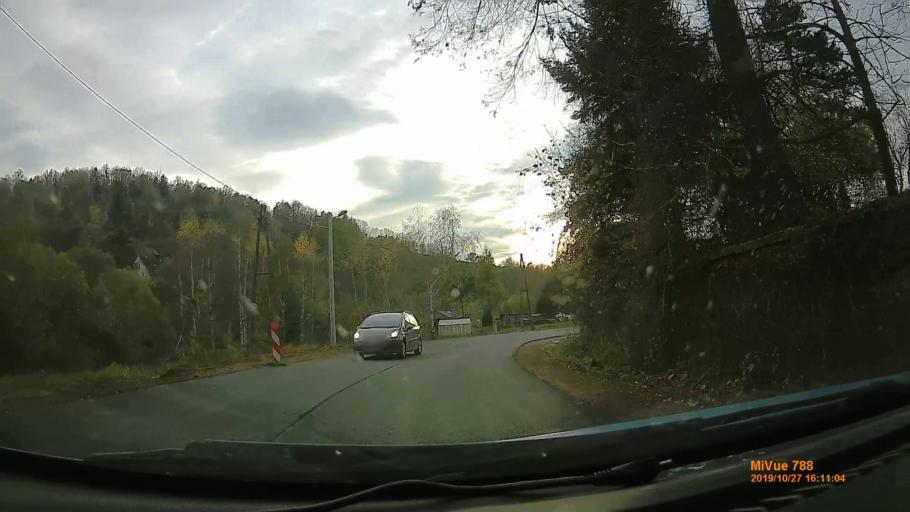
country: PL
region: Lower Silesian Voivodeship
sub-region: Powiat klodzki
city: Radkow
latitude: 50.5542
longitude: 16.4312
